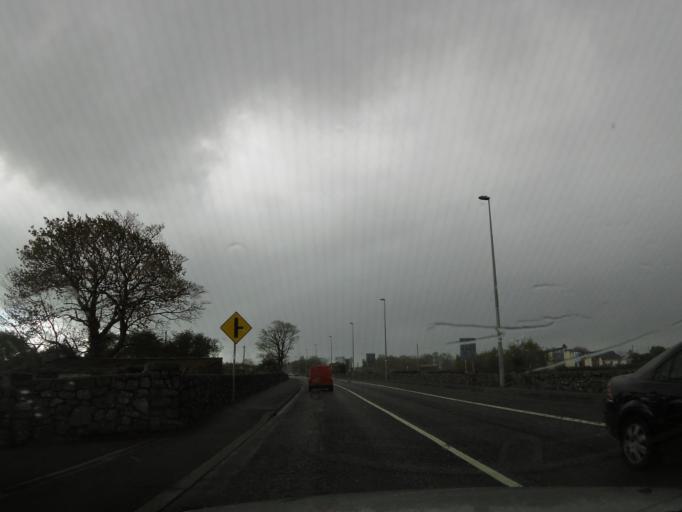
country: IE
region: Connaught
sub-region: County Galway
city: Claregalway
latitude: 53.3384
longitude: -8.9494
